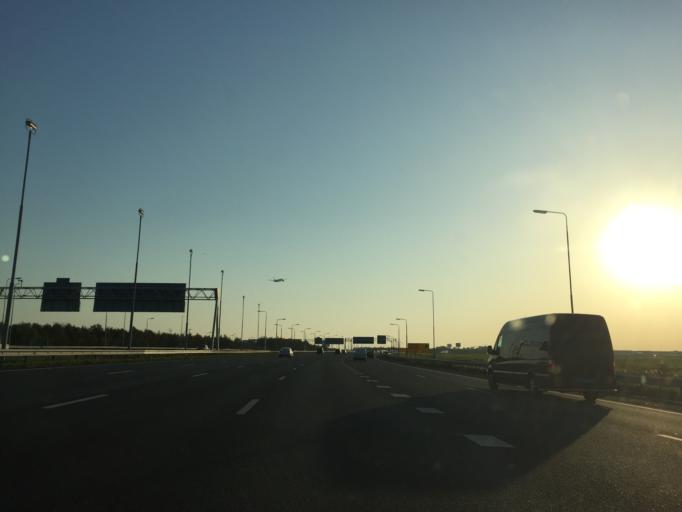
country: NL
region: North Holland
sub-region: Gemeente Aalsmeer
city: Aalsmeer
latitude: 52.2990
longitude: 4.7415
